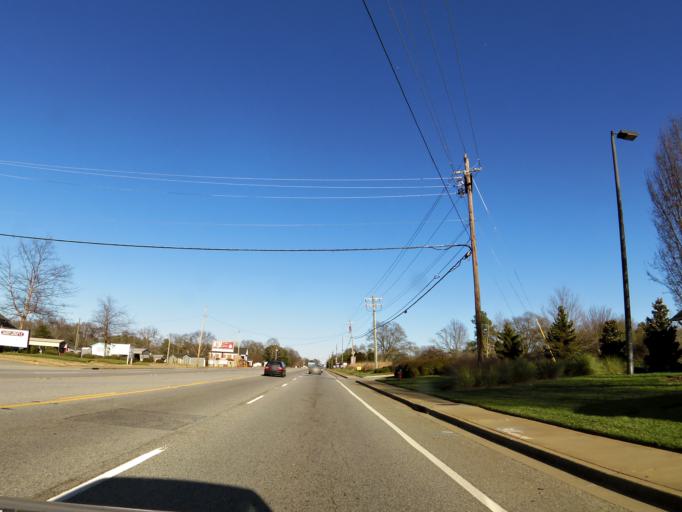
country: US
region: South Carolina
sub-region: Spartanburg County
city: Fairforest
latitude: 34.9130
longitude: -82.0127
